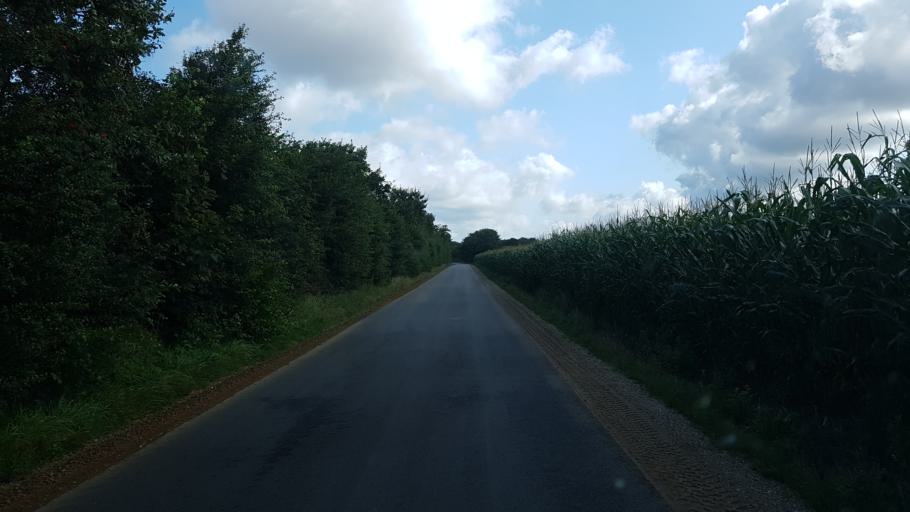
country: DK
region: South Denmark
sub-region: Varde Kommune
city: Olgod
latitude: 55.7809
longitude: 8.7202
